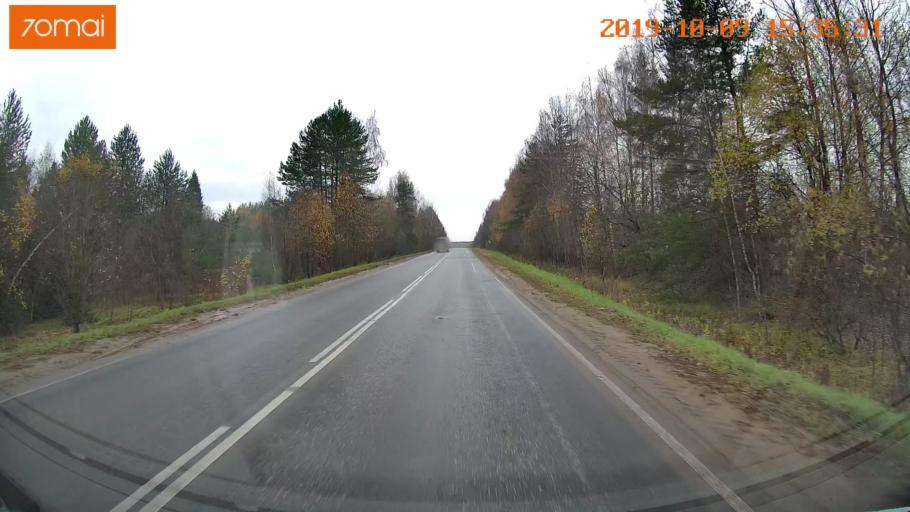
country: RU
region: Kostroma
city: Oktyabr'skiy
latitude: 57.9312
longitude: 41.2254
